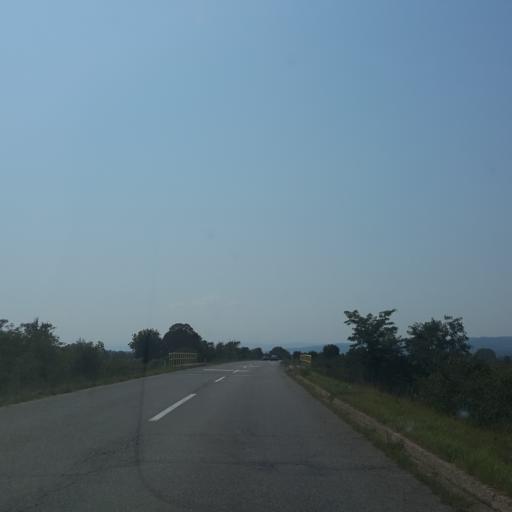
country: RS
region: Central Serbia
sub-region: Zajecarski Okrug
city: Knjazevac
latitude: 43.7061
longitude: 22.3034
